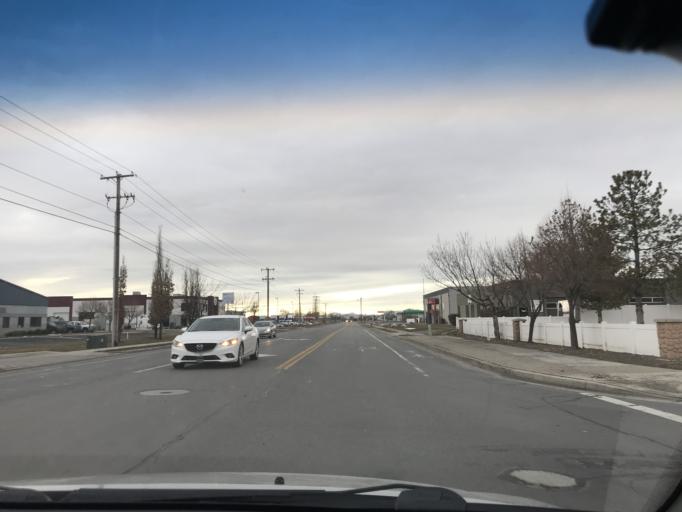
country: US
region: Utah
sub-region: Davis County
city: North Salt Lake
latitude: 40.8617
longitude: -111.9225
